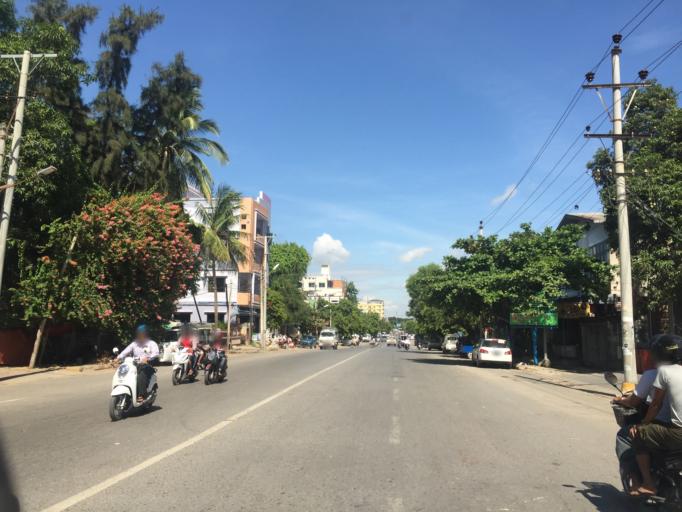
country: MM
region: Mandalay
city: Mandalay
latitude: 21.9840
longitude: 96.0686
